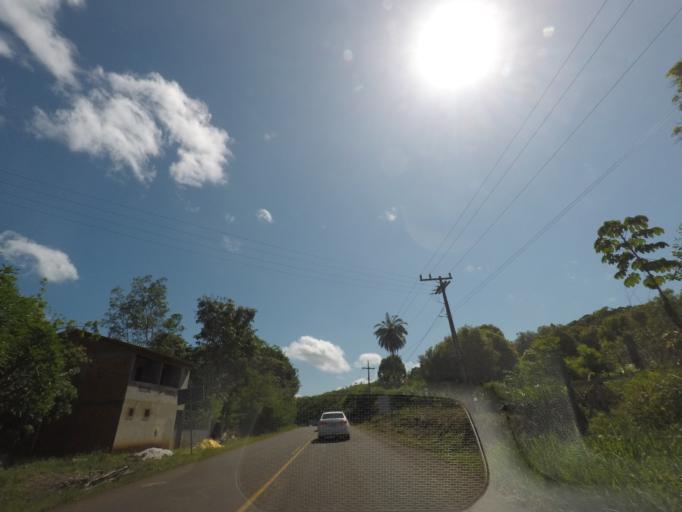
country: BR
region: Bahia
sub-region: Itubera
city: Itubera
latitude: -13.6905
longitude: -39.1322
